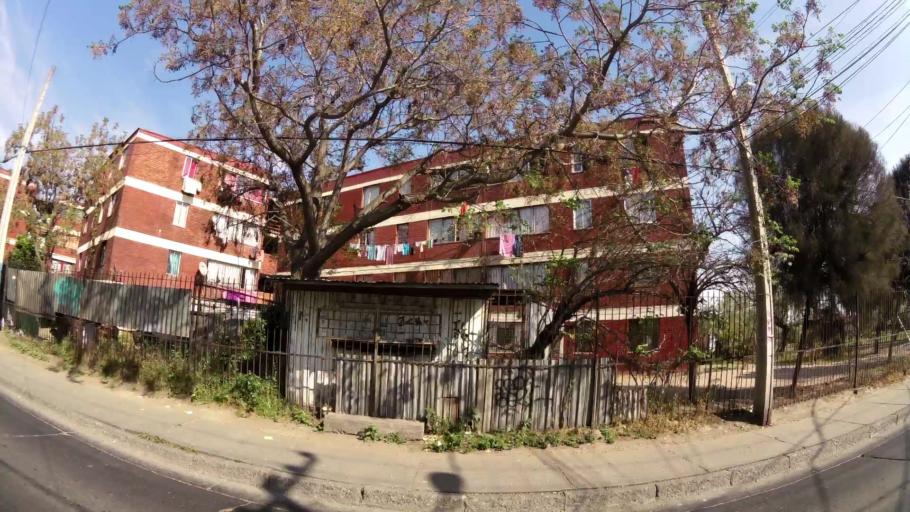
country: CL
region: Santiago Metropolitan
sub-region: Provincia de Santiago
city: La Pintana
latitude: -33.5595
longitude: -70.6618
